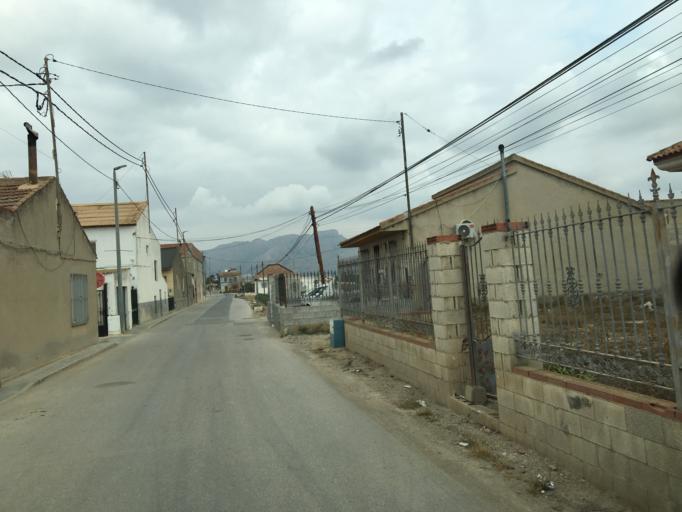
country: ES
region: Murcia
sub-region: Murcia
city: Beniel
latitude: 38.0399
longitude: -0.9890
